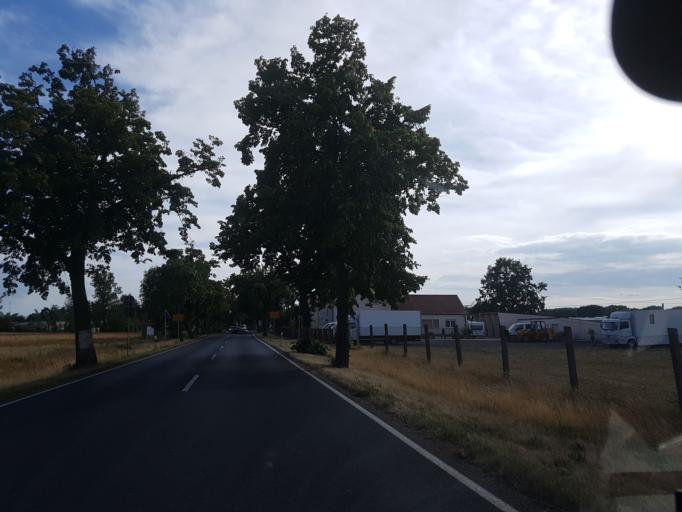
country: DE
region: Brandenburg
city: Herzberg
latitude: 51.7003
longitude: 13.2553
